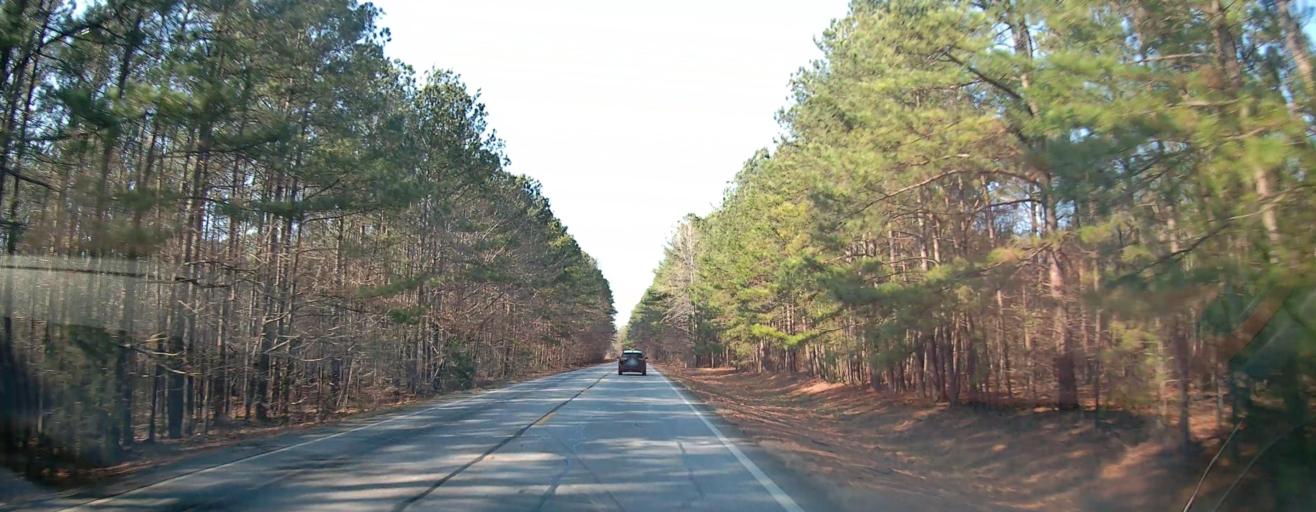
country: US
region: Georgia
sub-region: Butts County
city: Indian Springs
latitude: 33.2122
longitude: -83.8617
